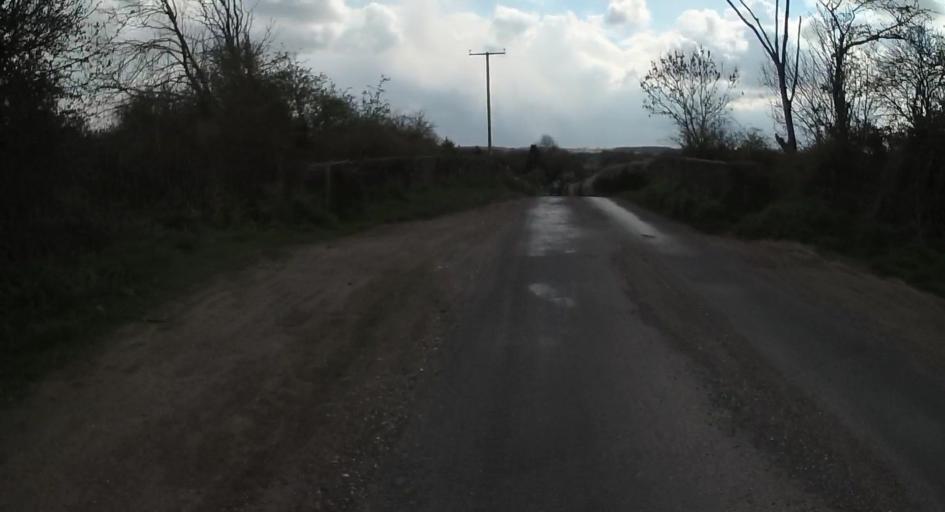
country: GB
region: England
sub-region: Hampshire
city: Kings Worthy
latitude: 51.0910
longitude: -1.2028
